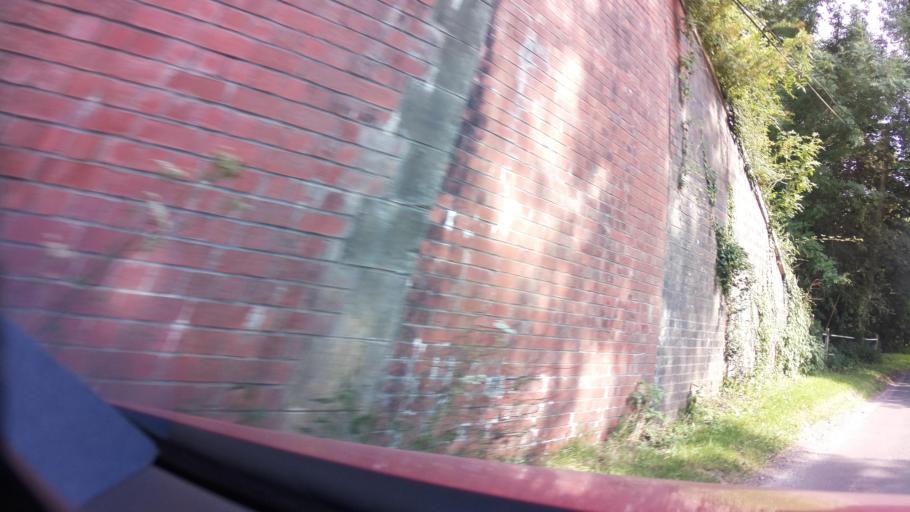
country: GB
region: England
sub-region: Wiltshire
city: Minety
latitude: 51.6201
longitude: -1.9664
